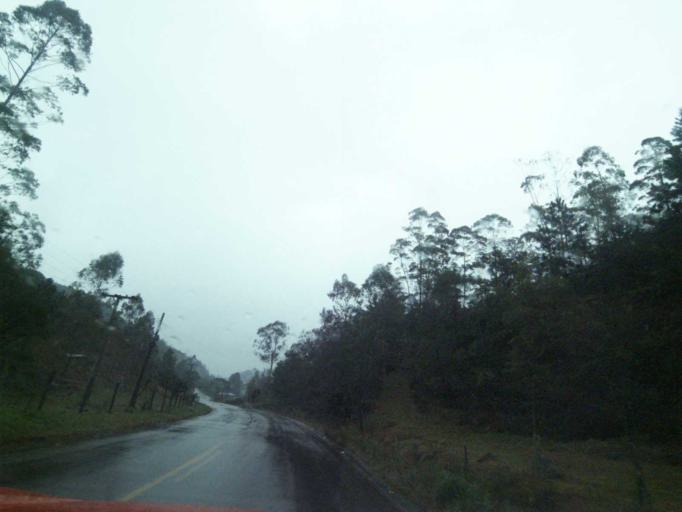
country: BR
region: Santa Catarina
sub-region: Anitapolis
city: Anitapolis
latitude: -27.8245
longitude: -49.0500
